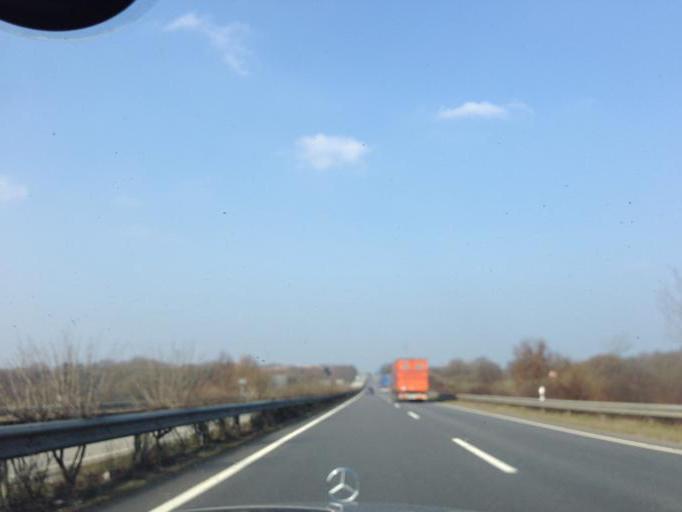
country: DE
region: Schleswig-Holstein
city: Hogersdorf
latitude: 53.9090
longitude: 10.2750
